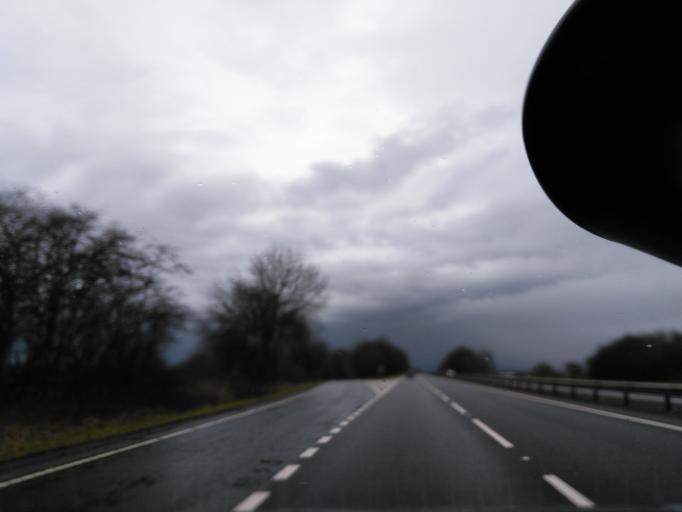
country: GB
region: England
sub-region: North Yorkshire
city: Thirsk
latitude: 54.1762
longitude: -1.3826
